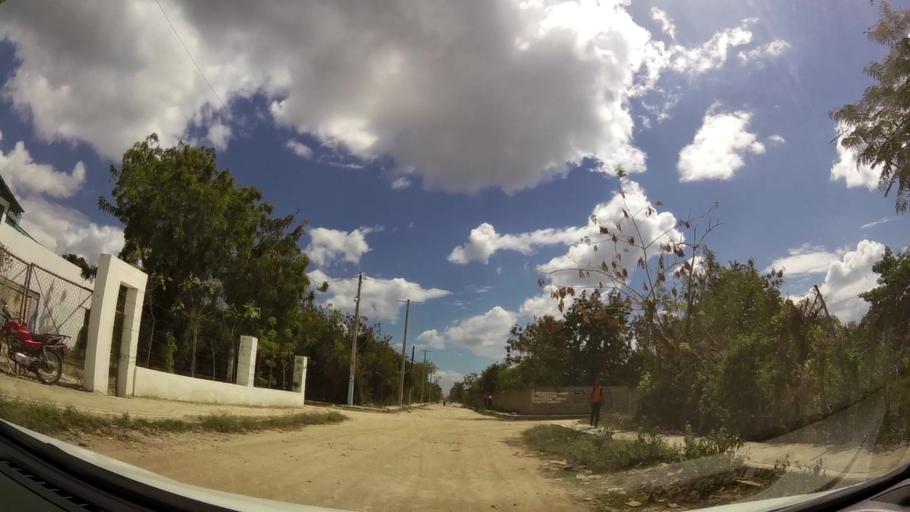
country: DO
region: Santo Domingo
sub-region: Santo Domingo
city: Boca Chica
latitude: 18.4531
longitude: -69.6549
